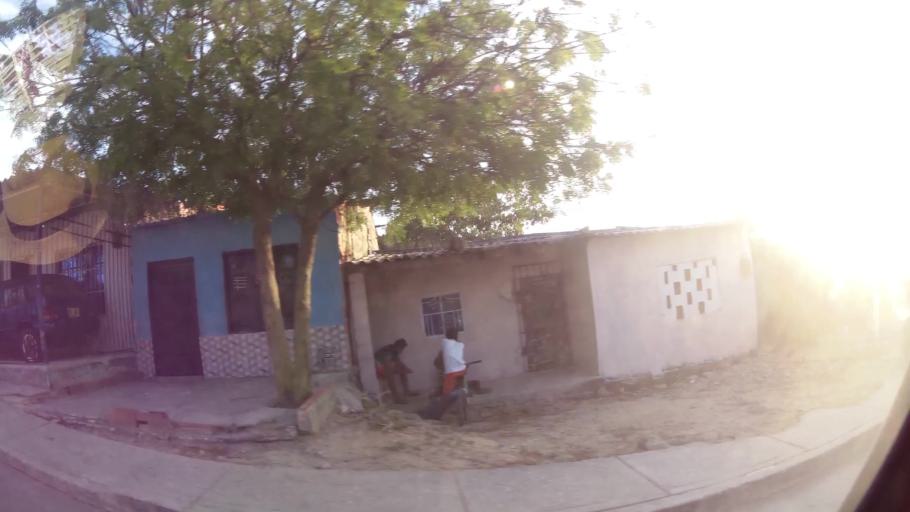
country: CO
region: Atlantico
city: Barranquilla
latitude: 10.9597
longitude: -74.8247
